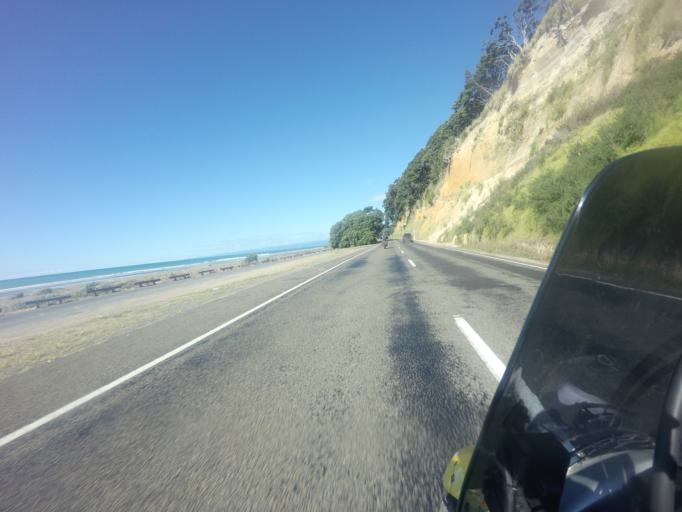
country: NZ
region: Bay of Plenty
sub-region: Opotiki District
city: Opotiki
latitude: -37.9912
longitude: 177.2121
